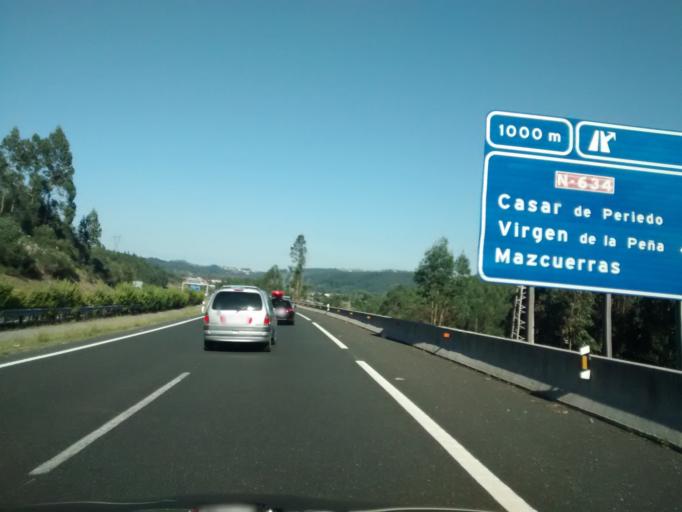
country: ES
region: Cantabria
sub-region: Provincia de Cantabria
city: Luzmela
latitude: 43.3213
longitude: -4.2063
